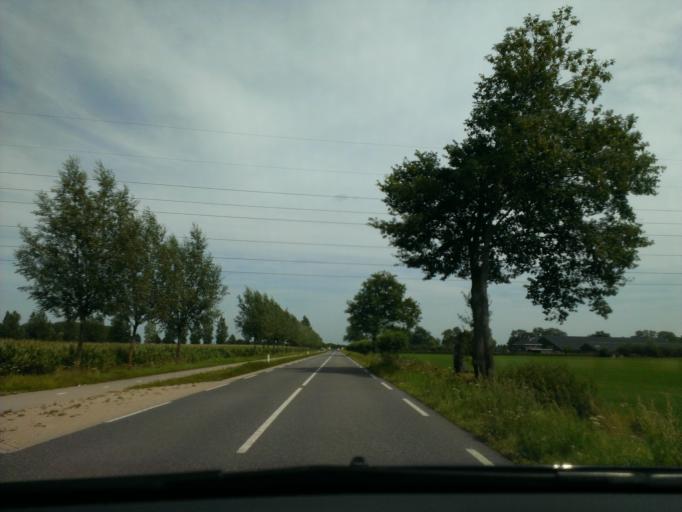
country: NL
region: Gelderland
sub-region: Gemeente Voorst
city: Twello
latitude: 52.2844
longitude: 6.0773
